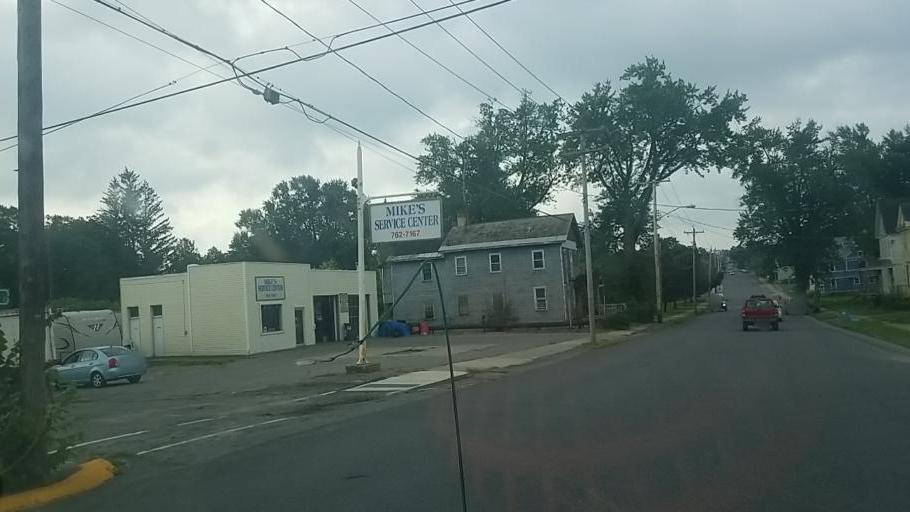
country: US
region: New York
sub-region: Fulton County
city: Johnstown
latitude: 43.0112
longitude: -74.3715
